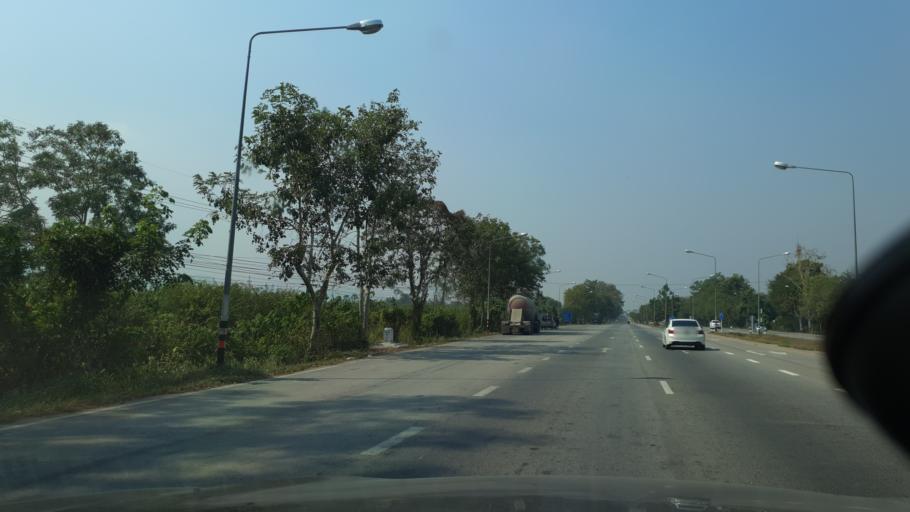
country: TH
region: Kamphaeng Phet
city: Kosamphi Nakhon
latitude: 16.6004
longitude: 99.4022
